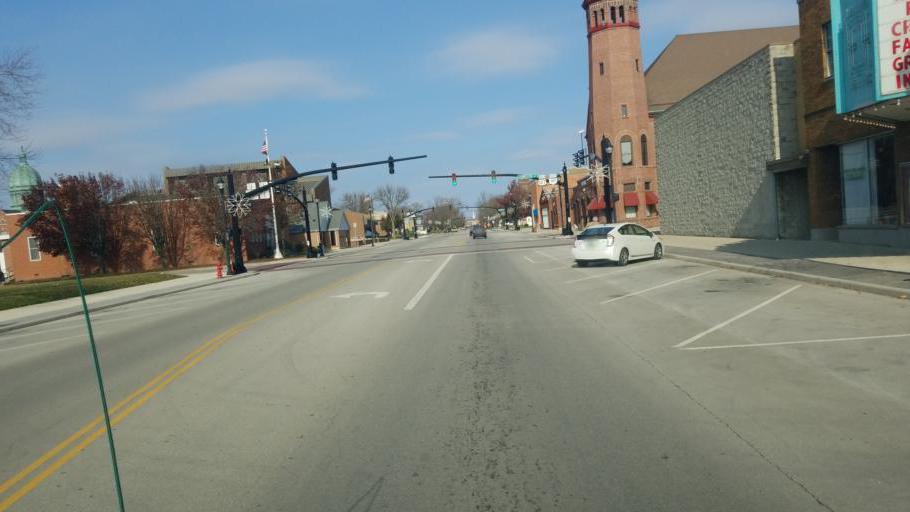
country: US
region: Ohio
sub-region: Mercer County
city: Celina
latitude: 40.5495
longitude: -84.5708
